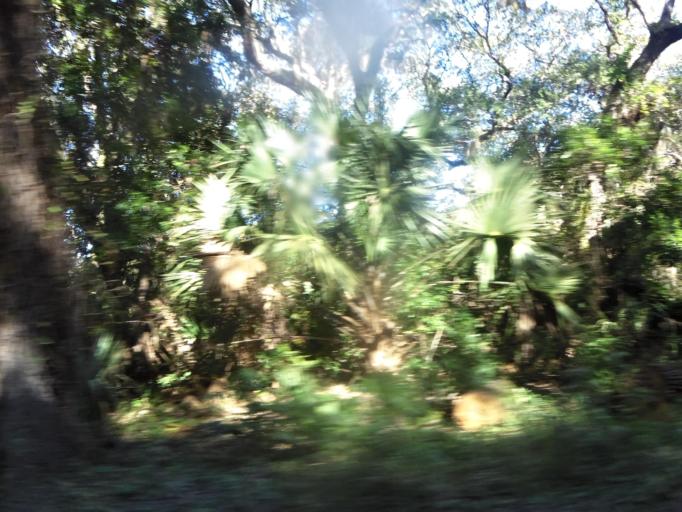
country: US
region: Florida
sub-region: Duval County
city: Atlantic Beach
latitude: 30.4329
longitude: -81.4291
